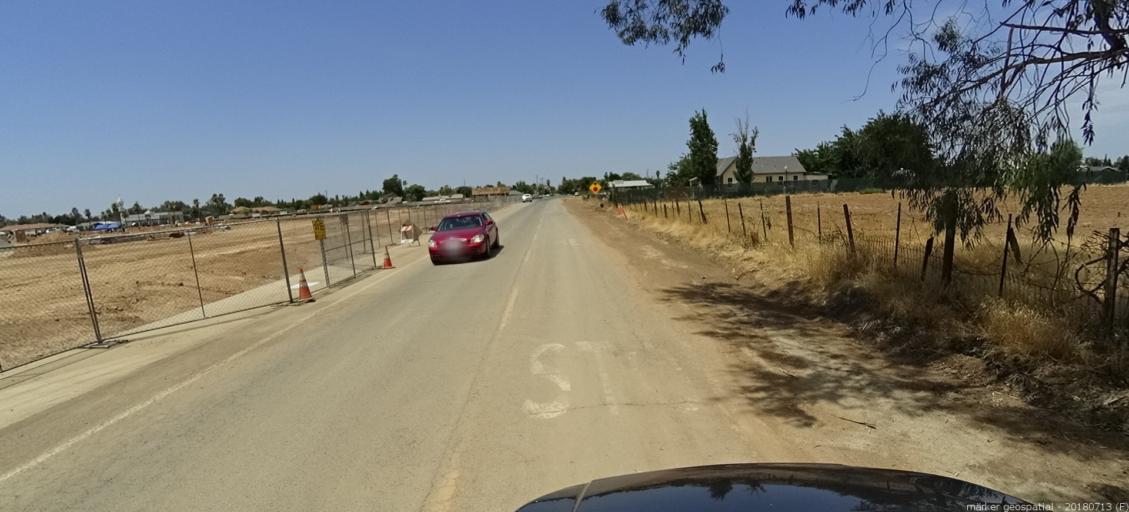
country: US
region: California
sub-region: Madera County
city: Madera Acres
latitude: 36.9927
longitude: -120.0720
